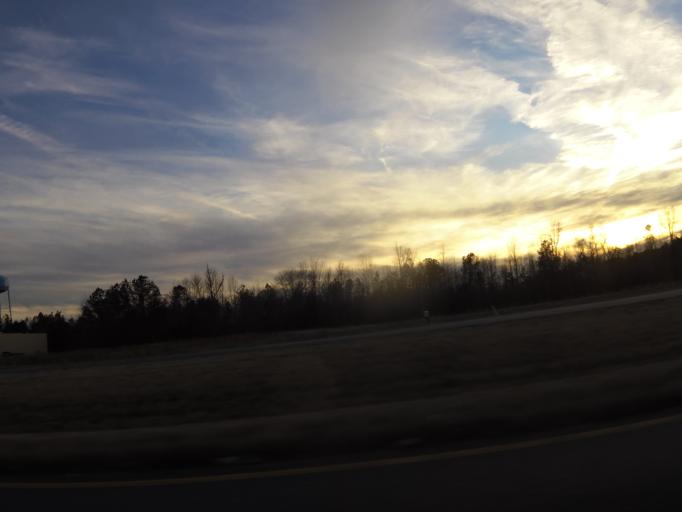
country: US
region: Virginia
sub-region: Southampton County
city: Courtland
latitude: 36.6881
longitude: -77.0254
